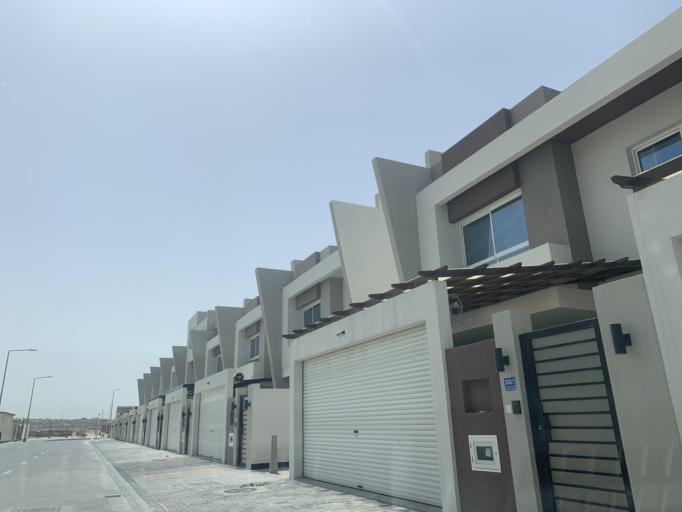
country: BH
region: Northern
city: Madinat `Isa
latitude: 26.1547
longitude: 50.5634
